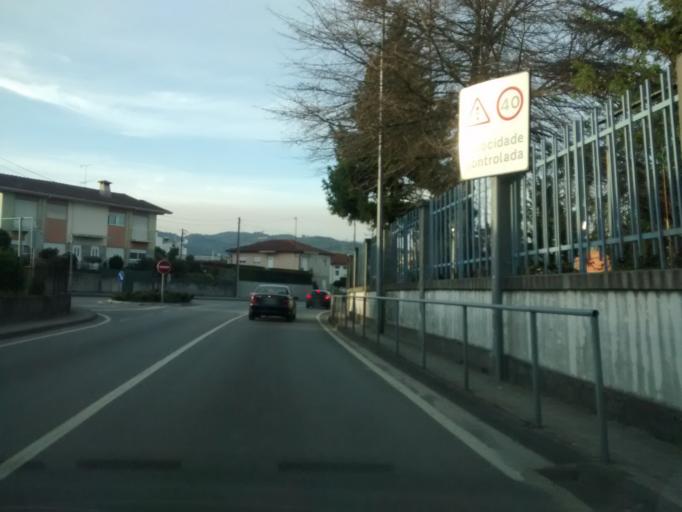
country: PT
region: Braga
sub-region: Guimaraes
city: Brito
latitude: 41.4843
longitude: -8.3535
